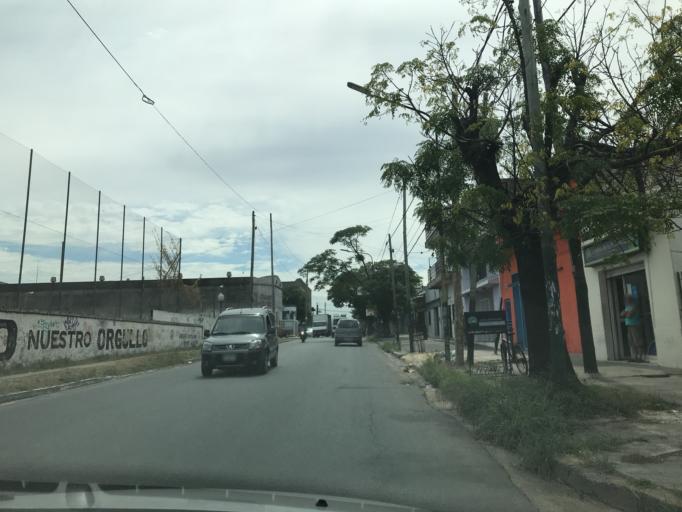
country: AR
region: Buenos Aires
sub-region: Partido de Lomas de Zamora
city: Lomas de Zamora
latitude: -34.7313
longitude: -58.4261
